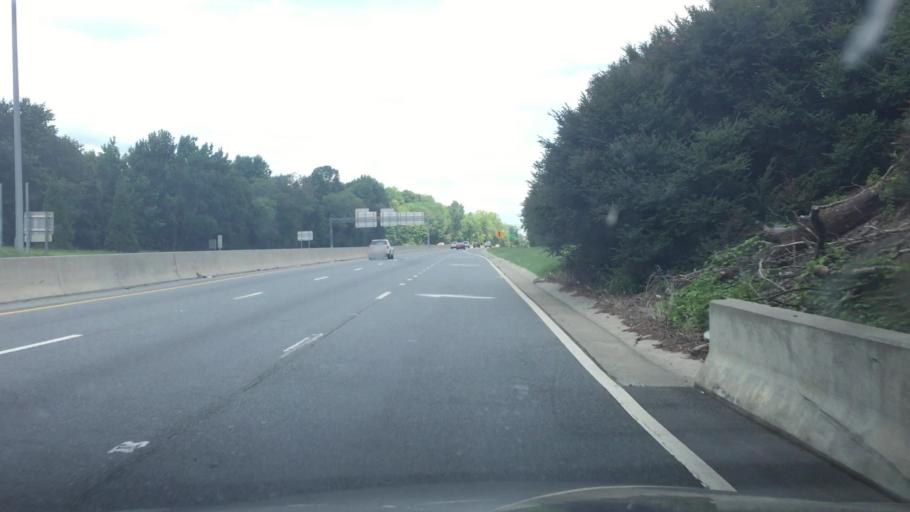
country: US
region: North Carolina
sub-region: Randolph County
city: Asheboro
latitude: 35.6877
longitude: -79.8307
